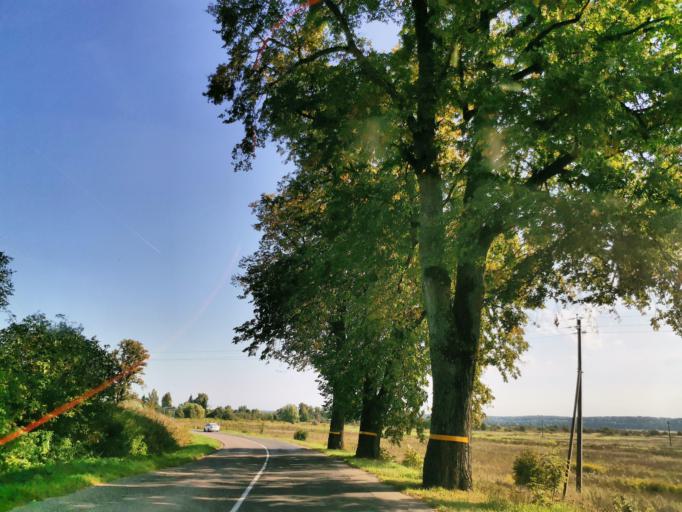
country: RU
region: Kaliningrad
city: Chernyakhovsk
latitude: 54.6922
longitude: 21.8590
